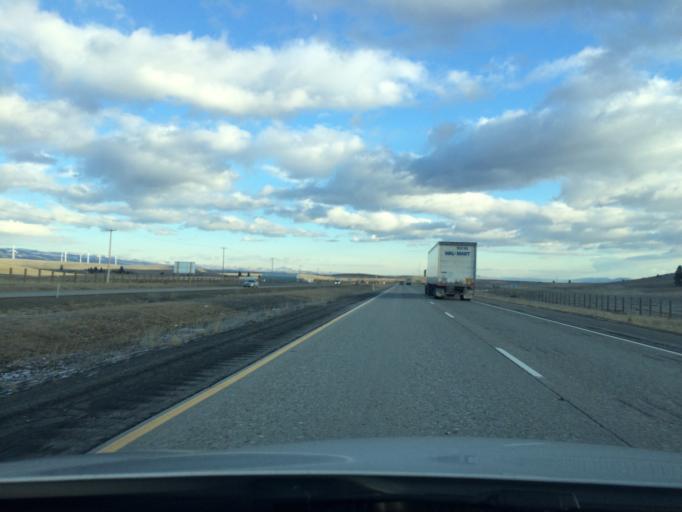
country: US
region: Washington
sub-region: Kittitas County
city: Cle Elum
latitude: 47.1116
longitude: -120.7815
